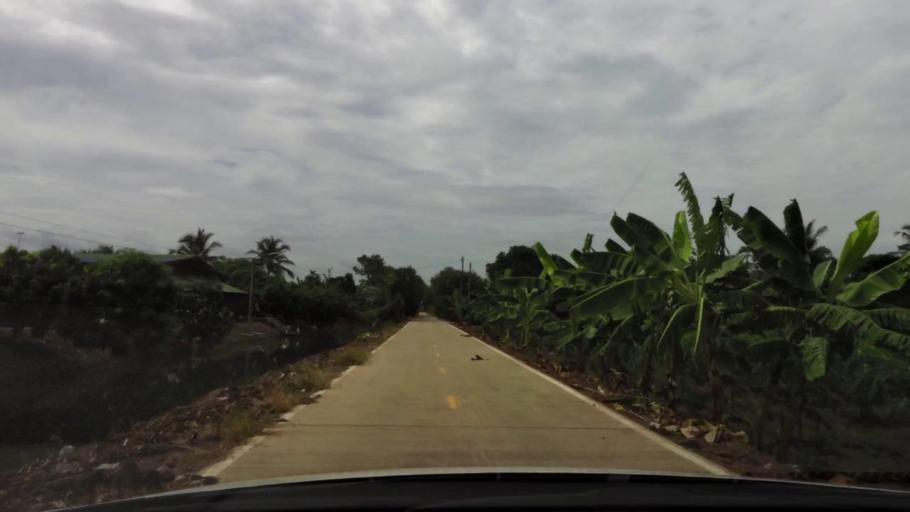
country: TH
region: Ratchaburi
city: Damnoen Saduak
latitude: 13.5485
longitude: 99.9837
